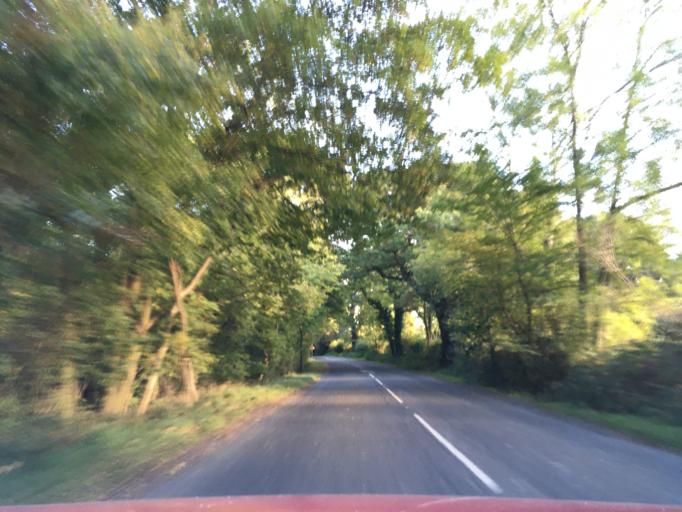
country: GB
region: England
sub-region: Herefordshire
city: Donnington
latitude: 52.0259
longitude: -2.3351
